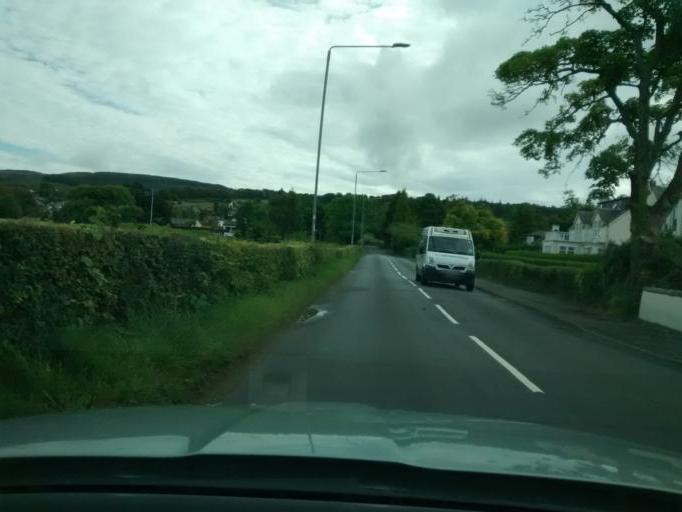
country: GB
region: Scotland
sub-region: North Ayrshire
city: Lamlash
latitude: 55.5795
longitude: -5.1568
